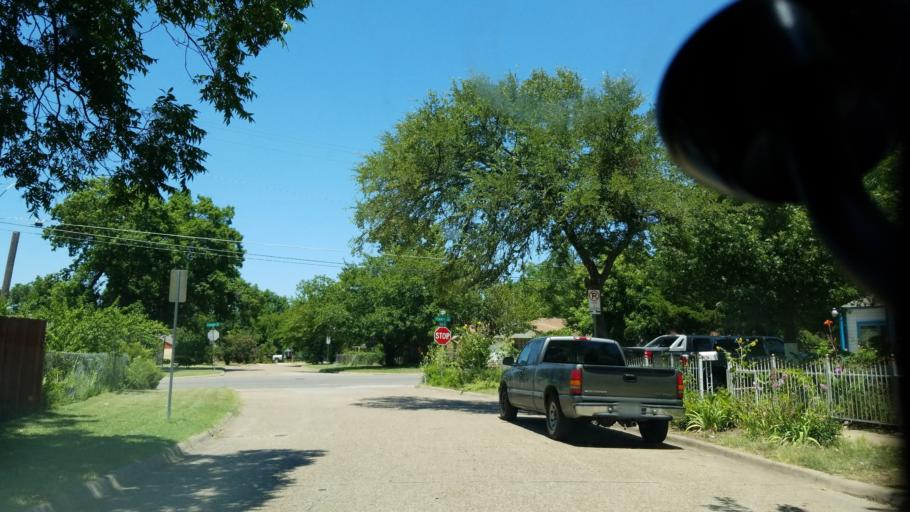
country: US
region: Texas
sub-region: Dallas County
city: Cockrell Hill
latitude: 32.7128
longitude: -96.8328
